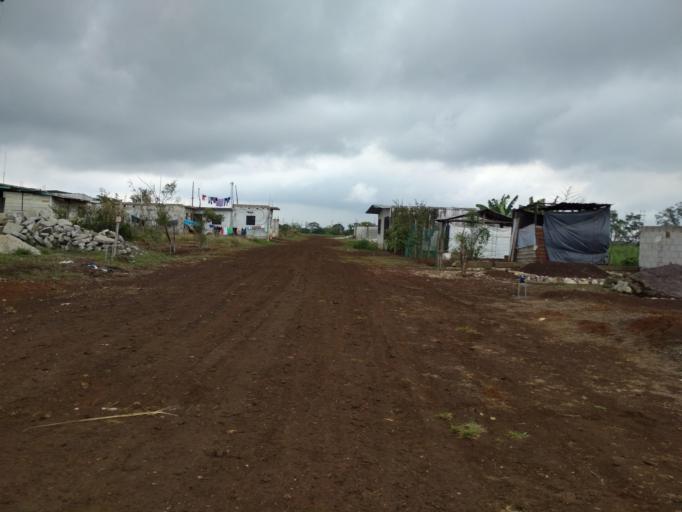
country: MX
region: Veracruz
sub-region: Cordoba
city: San Jose de Tapia
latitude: 18.8495
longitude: -96.9636
